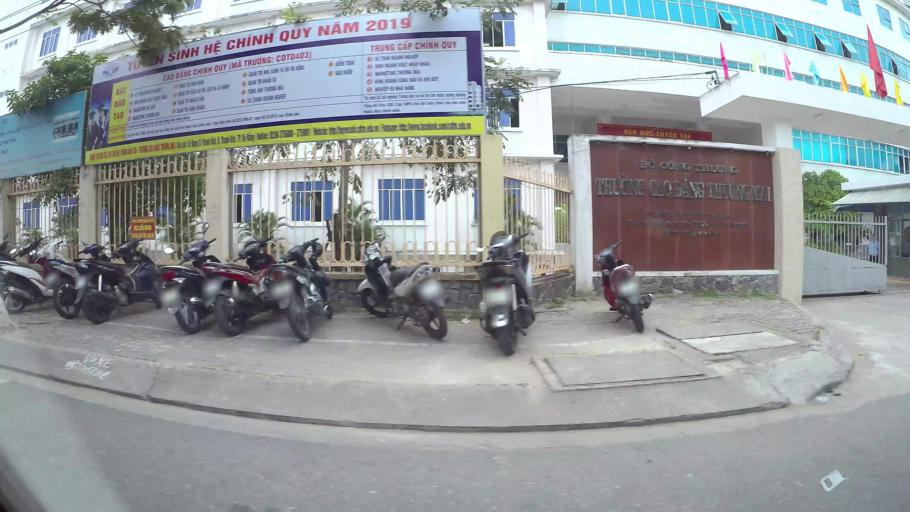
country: VN
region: Da Nang
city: Thanh Khe
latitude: 16.0721
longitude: 108.1787
